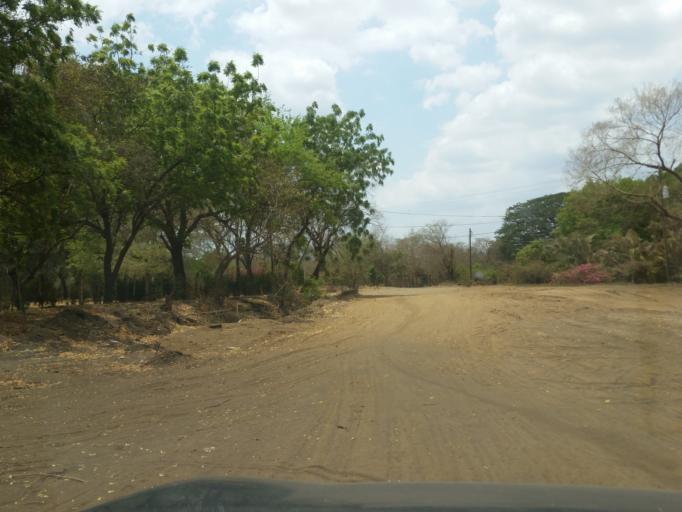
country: NI
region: Managua
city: Managua
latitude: 12.1344
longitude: -86.1634
